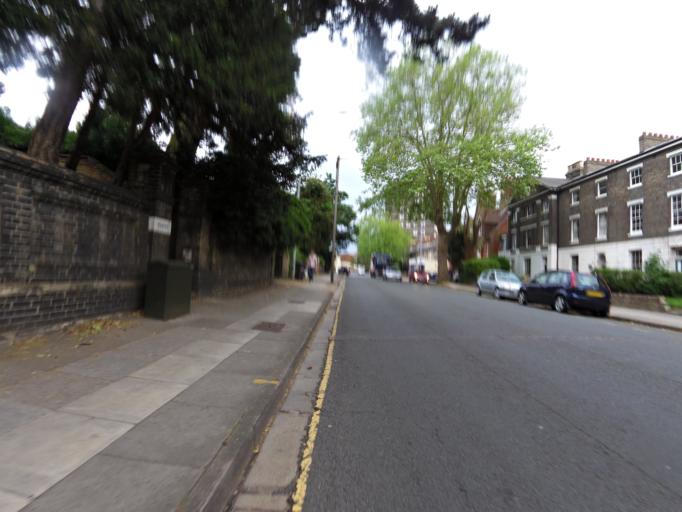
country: GB
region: England
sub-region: Suffolk
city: Ipswich
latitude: 52.0633
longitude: 1.1416
